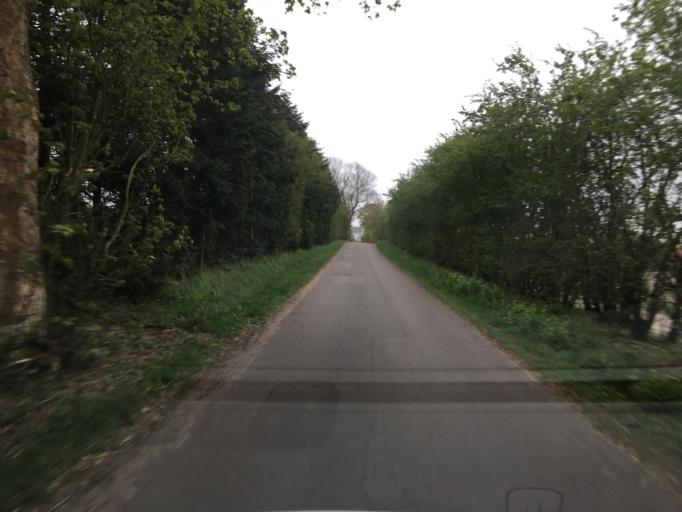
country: DK
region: South Denmark
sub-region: Aabenraa Kommune
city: Krusa
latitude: 54.8871
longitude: 9.3989
